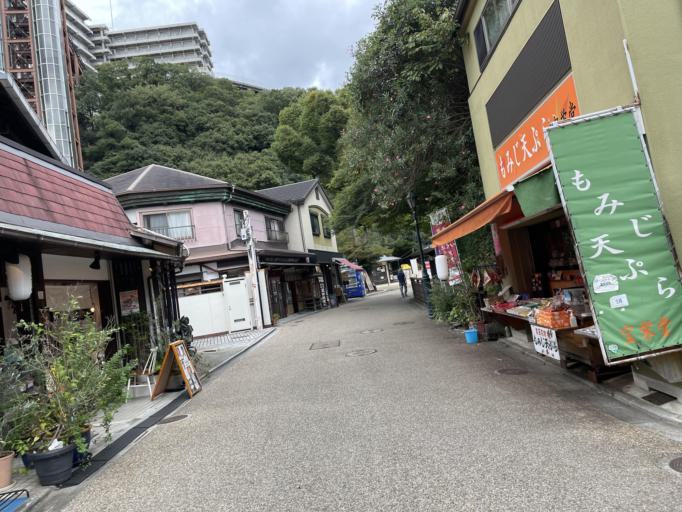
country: JP
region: Osaka
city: Mino
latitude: 34.8371
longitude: 135.4682
